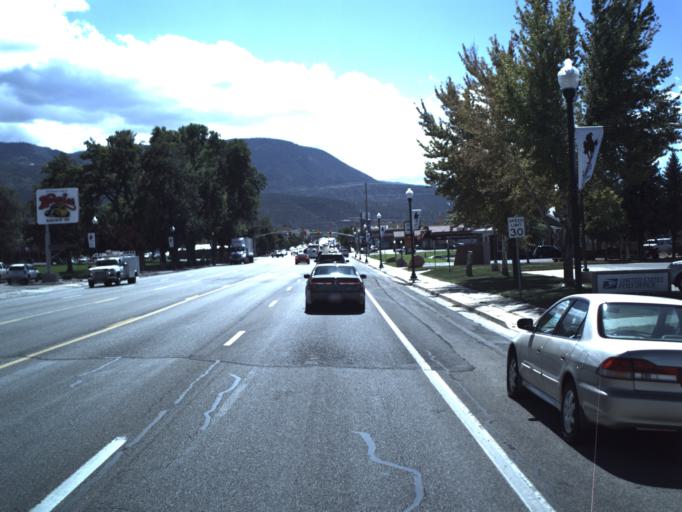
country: US
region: Utah
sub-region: Iron County
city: Cedar City
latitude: 37.6831
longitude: -113.0619
